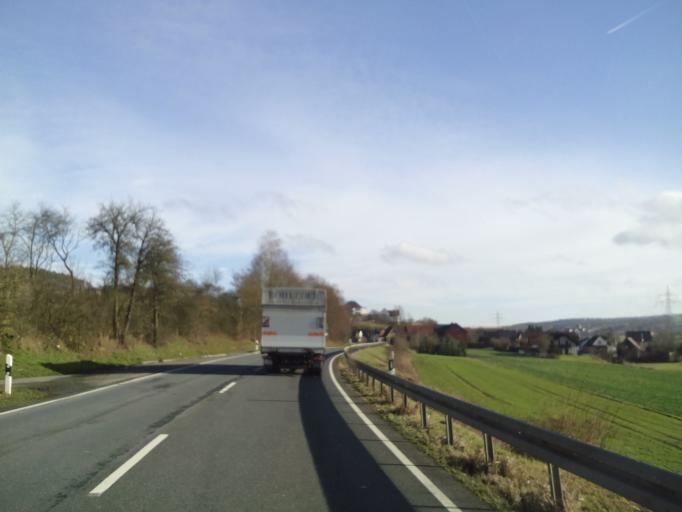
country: DE
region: Bavaria
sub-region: Upper Franconia
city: Altenkunstadt
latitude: 50.1283
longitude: 11.2753
